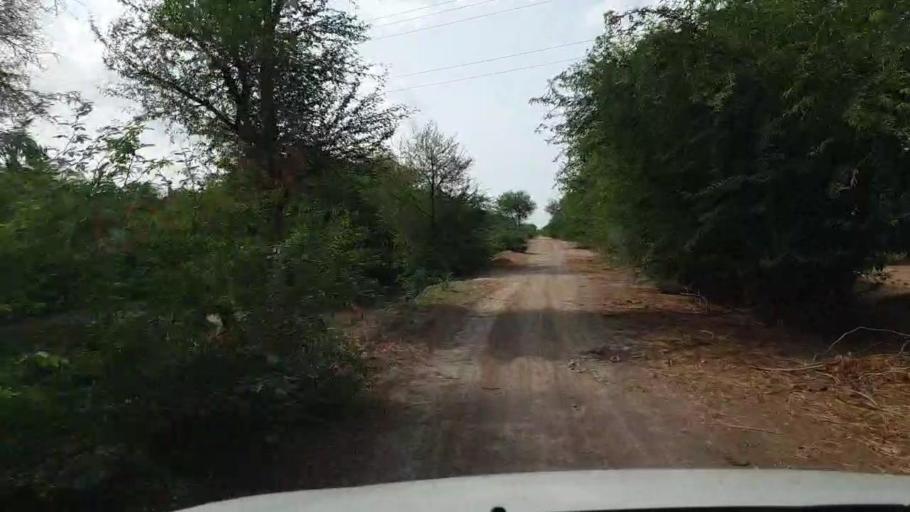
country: PK
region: Sindh
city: Kario
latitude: 24.7219
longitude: 68.6374
